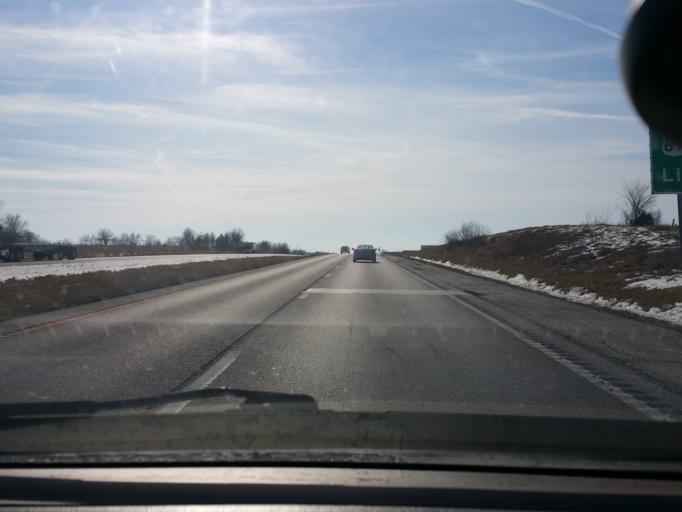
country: US
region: Missouri
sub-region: Clinton County
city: Cameron
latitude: 39.7213
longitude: -94.2224
